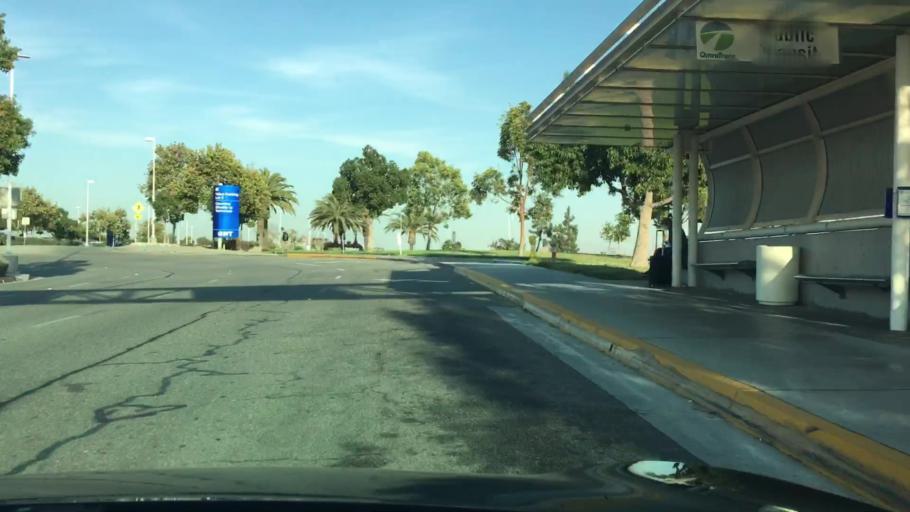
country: US
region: California
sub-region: San Bernardino County
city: Rancho Cucamonga
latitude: 34.0608
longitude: -117.5854
